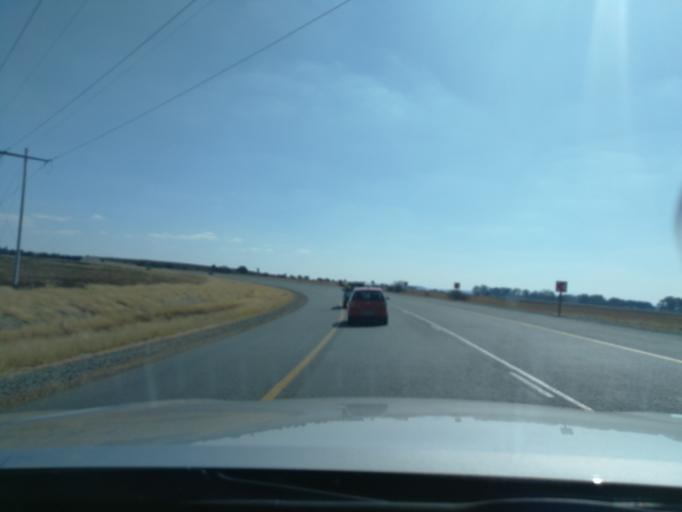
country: ZA
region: North-West
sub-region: Dr Kenneth Kaunda District Municipality
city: Klerksdorp
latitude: -26.8689
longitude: 26.6073
